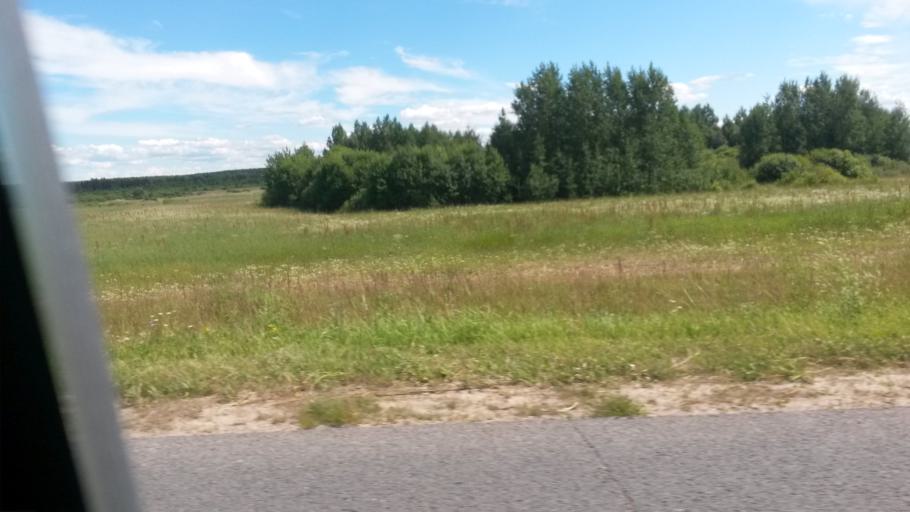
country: RU
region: Ivanovo
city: Staraya Vichuga
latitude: 57.2421
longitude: 41.8904
